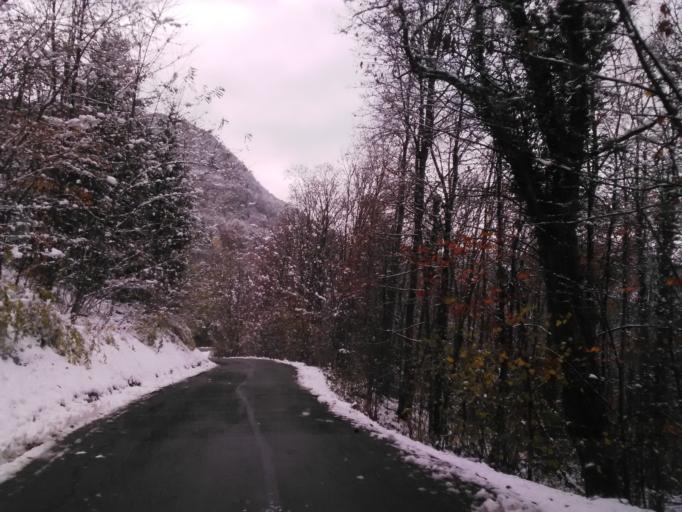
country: IT
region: Piedmont
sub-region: Provincia di Vercelli
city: Varallo
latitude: 45.7986
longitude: 8.2576
